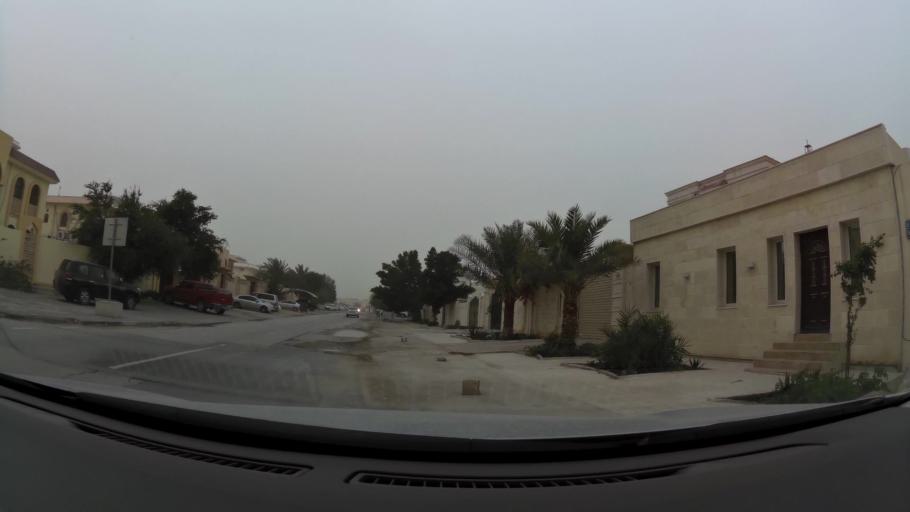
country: QA
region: Baladiyat ad Dawhah
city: Doha
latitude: 25.2327
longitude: 51.4978
